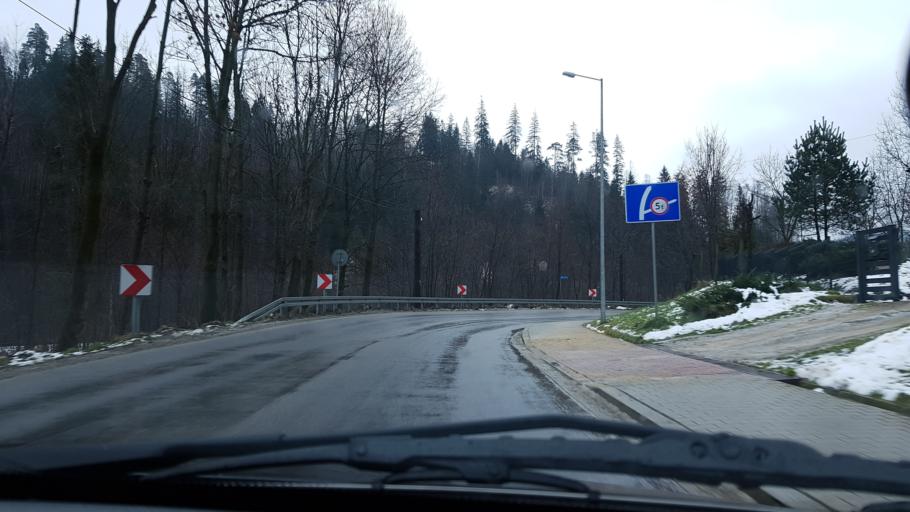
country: PL
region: Lesser Poland Voivodeship
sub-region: Powiat nowotarski
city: Raba Wyzna
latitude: 49.5437
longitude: 19.8923
